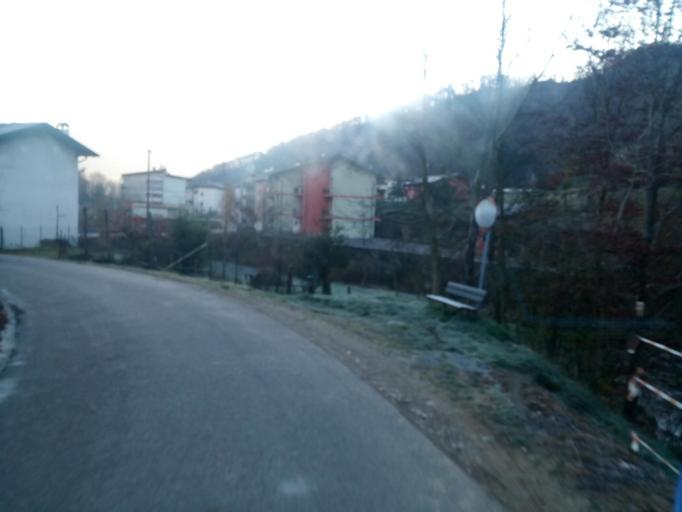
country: IT
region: Veneto
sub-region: Provincia di Vicenza
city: Valli del Pasubio
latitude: 45.7451
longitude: 11.2374
